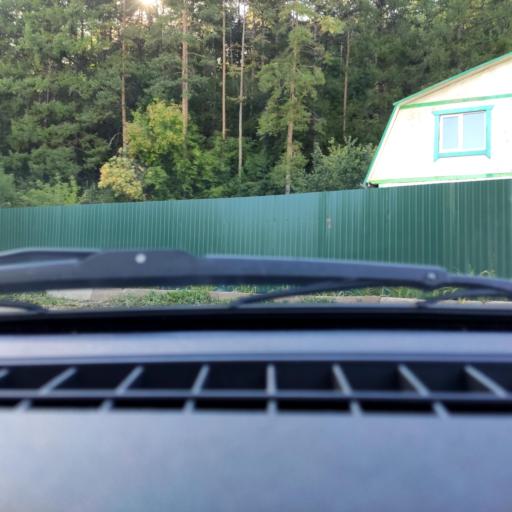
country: RU
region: Bashkortostan
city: Ufa
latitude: 54.8117
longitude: 56.1474
